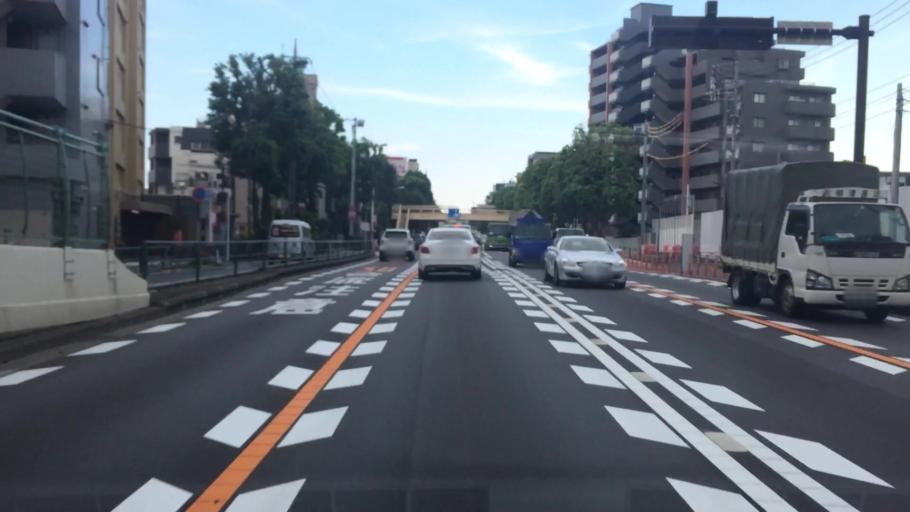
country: JP
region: Tokyo
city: Tokyo
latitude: 35.7178
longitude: 139.6538
